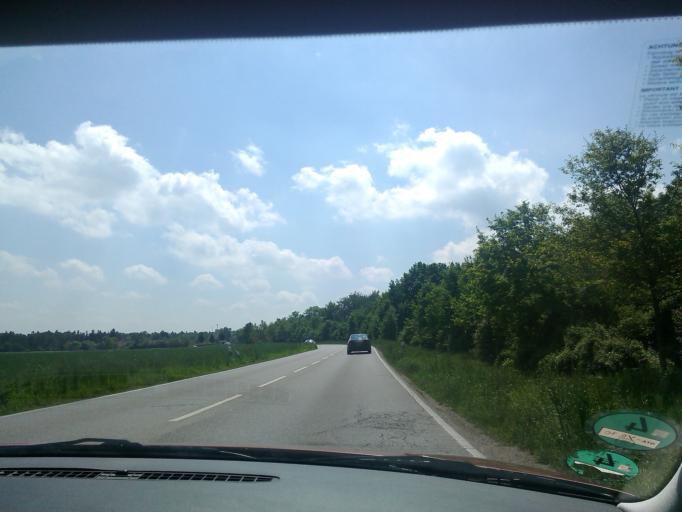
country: DE
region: Bavaria
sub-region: Upper Bavaria
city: Olching
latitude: 48.1830
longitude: 11.3298
